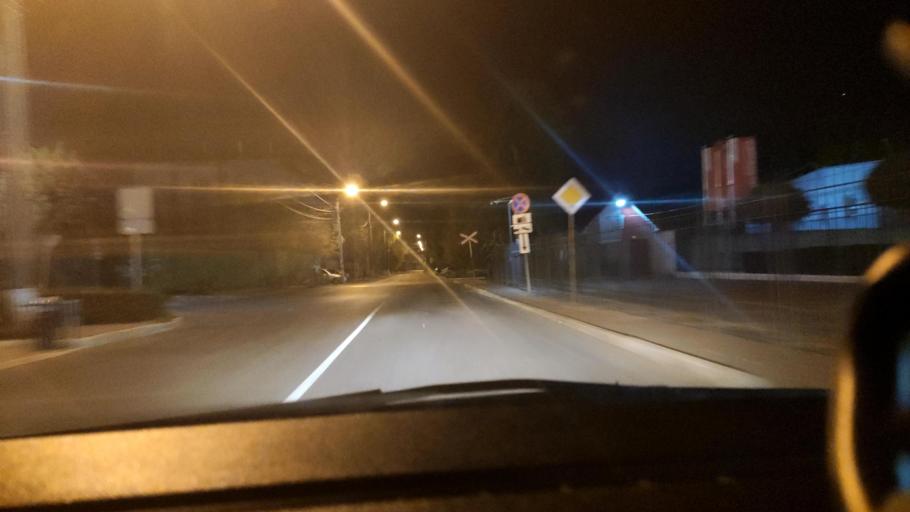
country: RU
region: Voronezj
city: Voronezh
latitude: 51.6851
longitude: 39.1700
